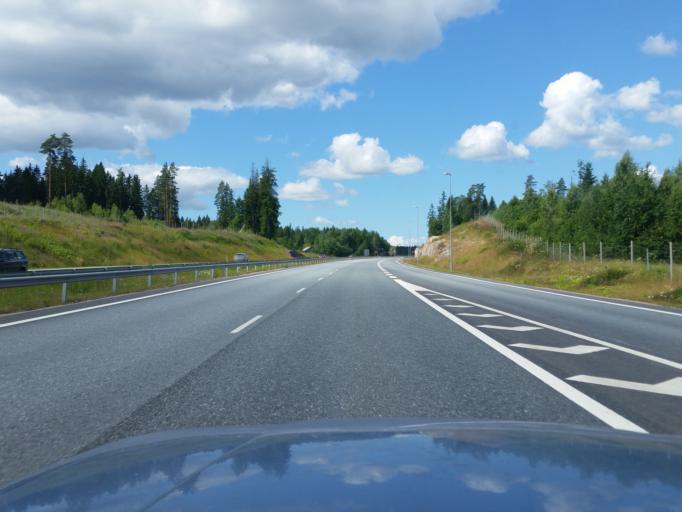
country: FI
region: Uusimaa
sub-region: Helsinki
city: Sammatti
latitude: 60.3790
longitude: 23.7970
